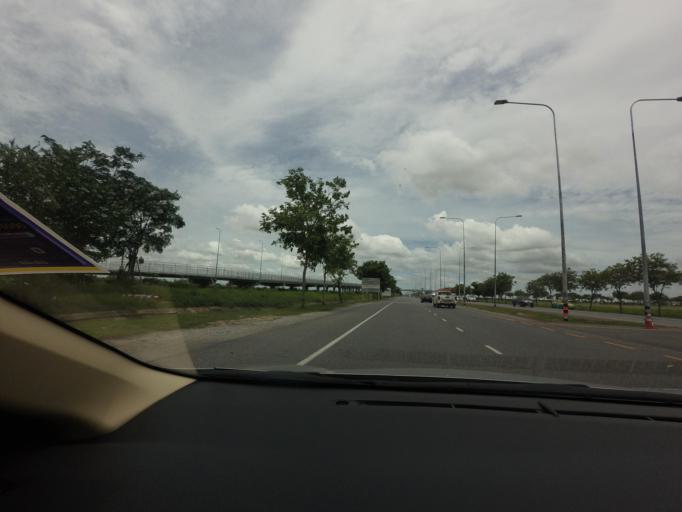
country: TH
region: Bangkok
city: Lat Krabang
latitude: 13.7103
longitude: 100.7753
